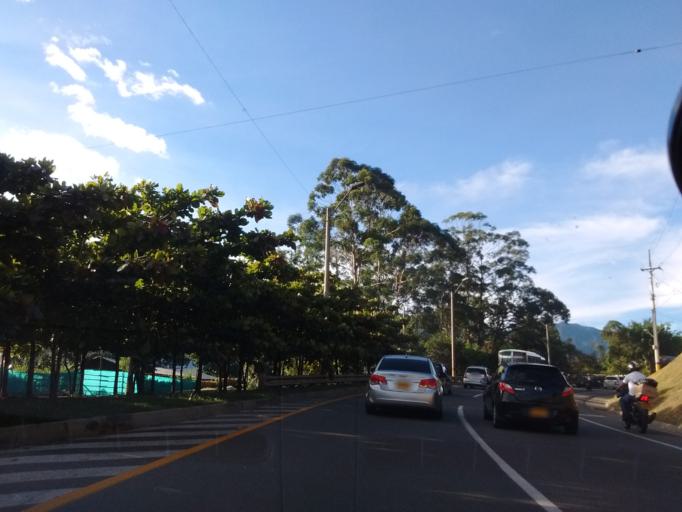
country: CO
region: Antioquia
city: Bello
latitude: 6.3128
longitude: -75.5497
